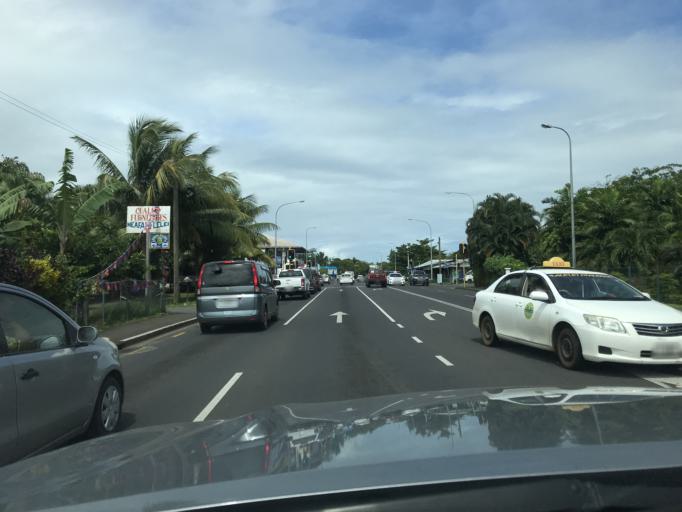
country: WS
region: Tuamasaga
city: Apia
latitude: -13.8385
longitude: -171.7741
